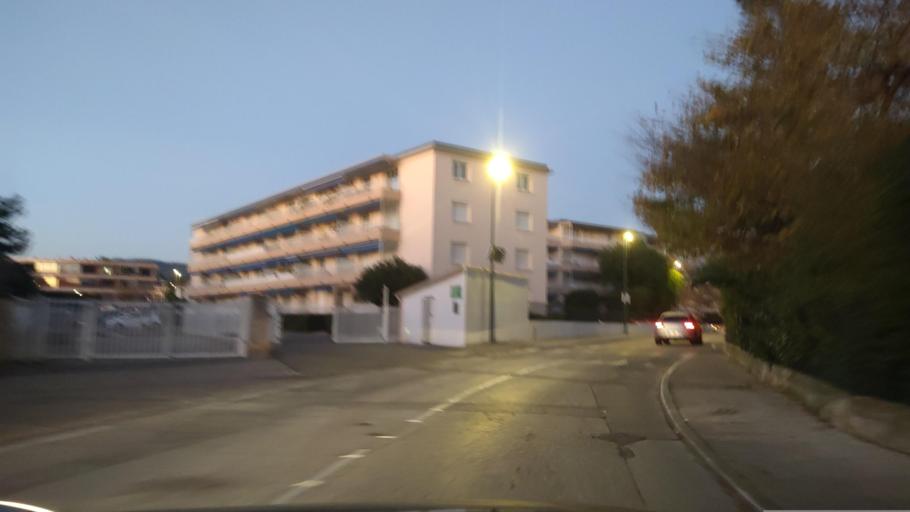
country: FR
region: Provence-Alpes-Cote d'Azur
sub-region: Departement du Var
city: Sanary-sur-Mer
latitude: 43.1178
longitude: 5.8119
